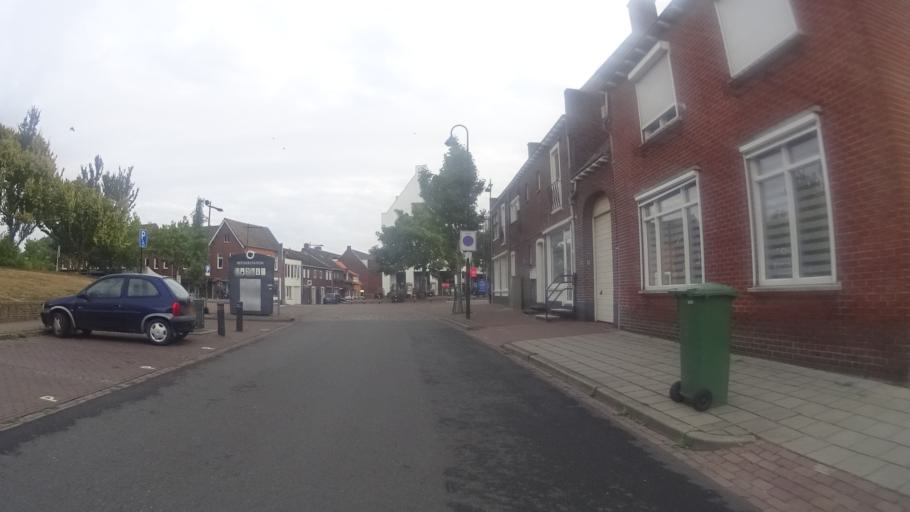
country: NL
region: Limburg
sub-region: Gemeente Venlo
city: Venlo
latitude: 51.4143
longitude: 6.1644
